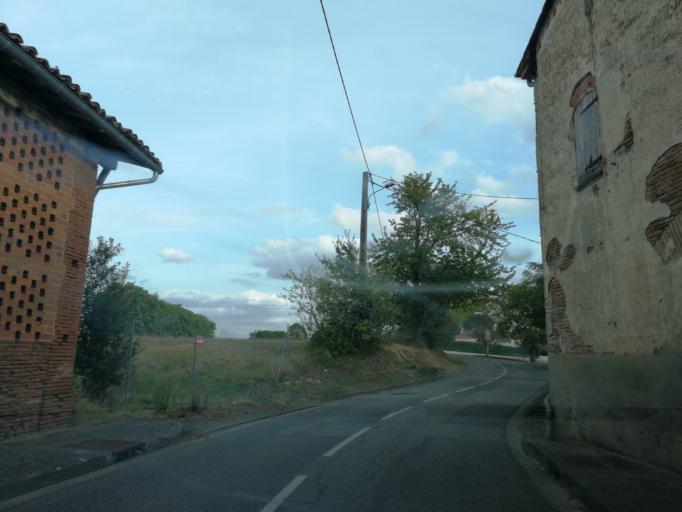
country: FR
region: Midi-Pyrenees
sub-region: Departement de la Haute-Garonne
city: Flourens
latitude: 43.5925
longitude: 1.5754
